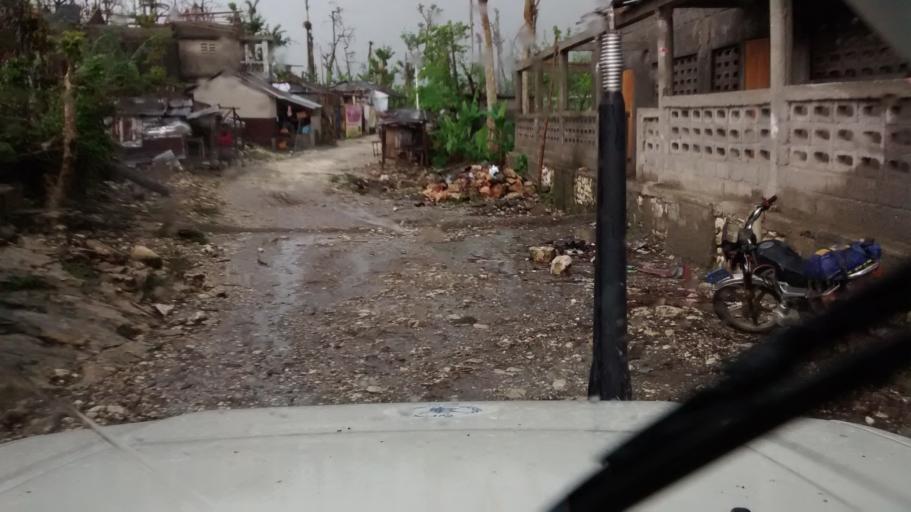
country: HT
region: Grandans
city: Moron
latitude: 18.5366
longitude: -74.1571
